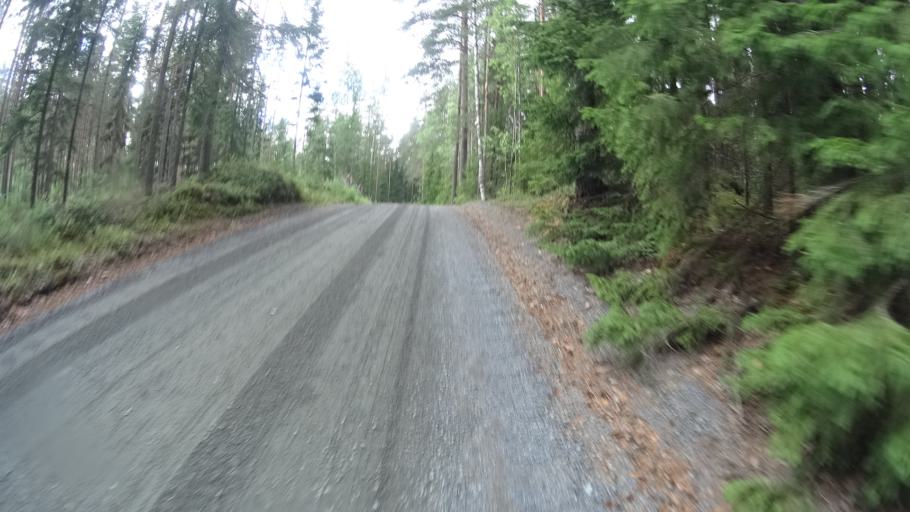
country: FI
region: Uusimaa
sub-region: Helsinki
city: Karkkila
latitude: 60.6020
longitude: 24.1800
